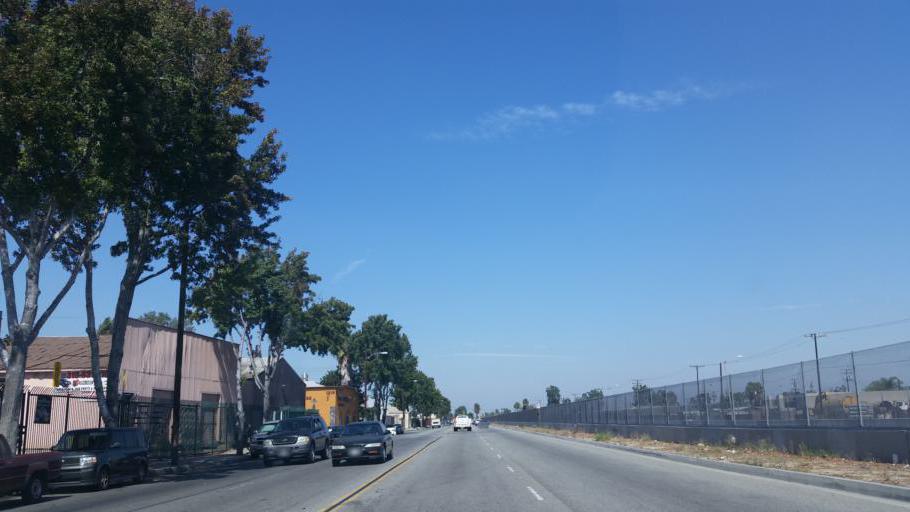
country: US
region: California
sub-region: Los Angeles County
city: Compton
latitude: 33.8839
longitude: -118.2185
